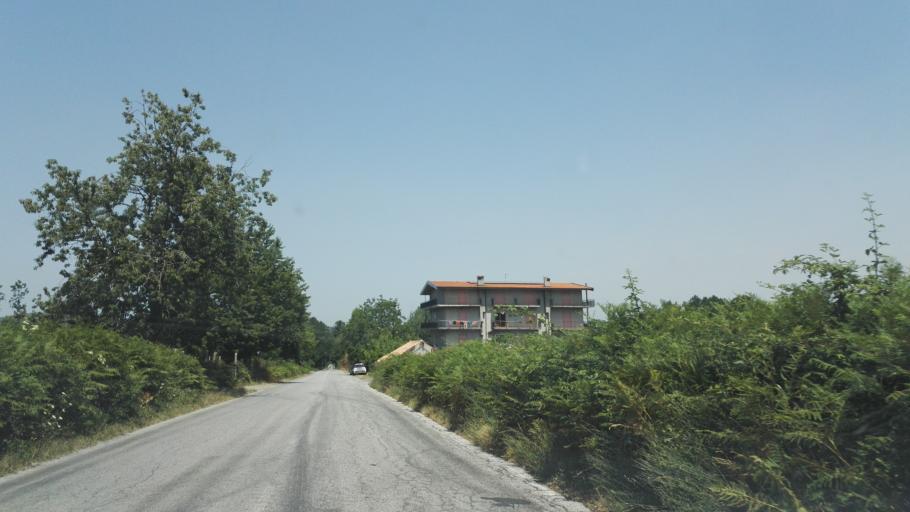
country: IT
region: Calabria
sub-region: Provincia di Vibo-Valentia
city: Serra San Bruno
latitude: 38.5570
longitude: 16.3265
